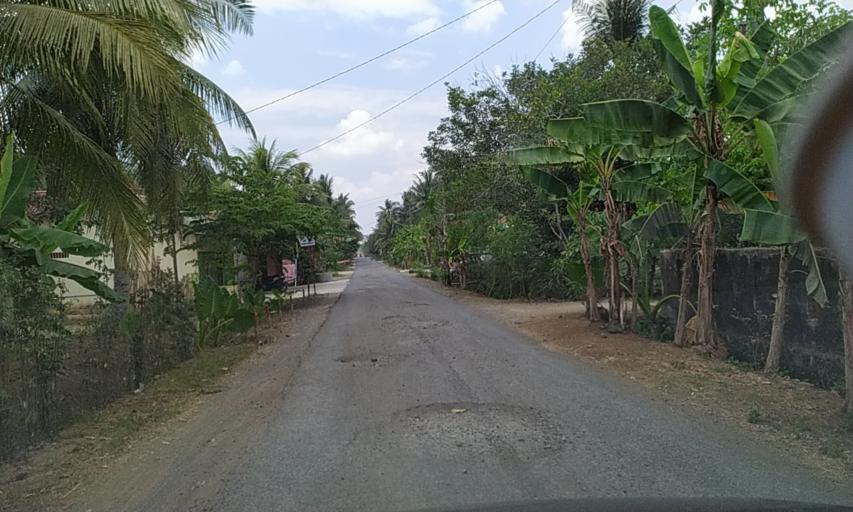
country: ID
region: Central Java
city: Sidaurip
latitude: -7.5538
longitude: 108.7561
